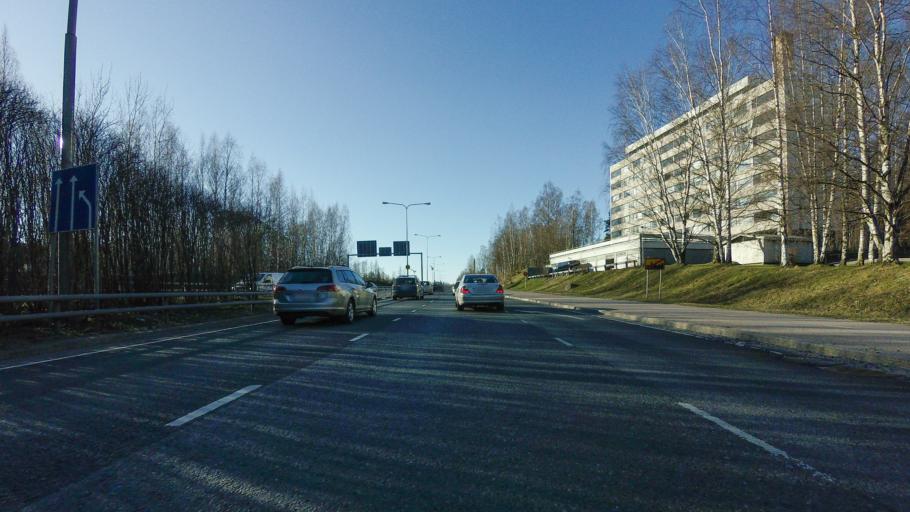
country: FI
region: Uusimaa
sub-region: Helsinki
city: Vantaa
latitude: 60.2150
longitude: 25.0855
